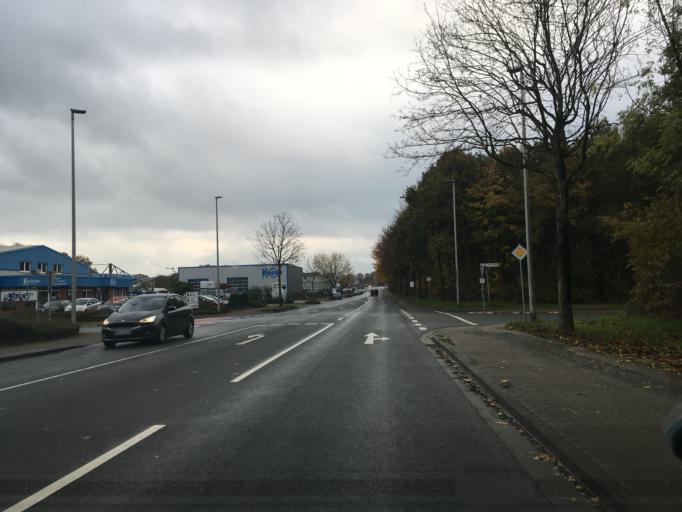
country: DE
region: North Rhine-Westphalia
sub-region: Regierungsbezirk Munster
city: Borken
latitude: 51.8607
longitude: 6.8742
